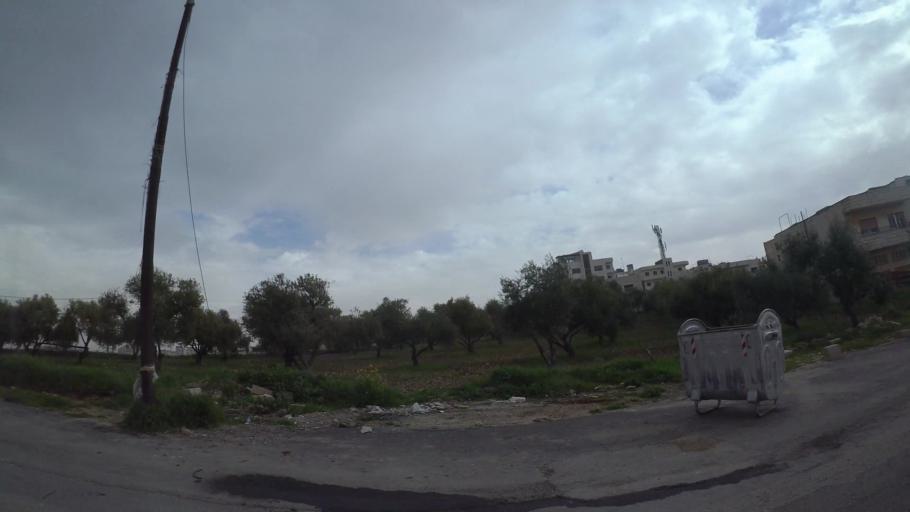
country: JO
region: Amman
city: Umm as Summaq
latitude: 31.9058
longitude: 35.8370
